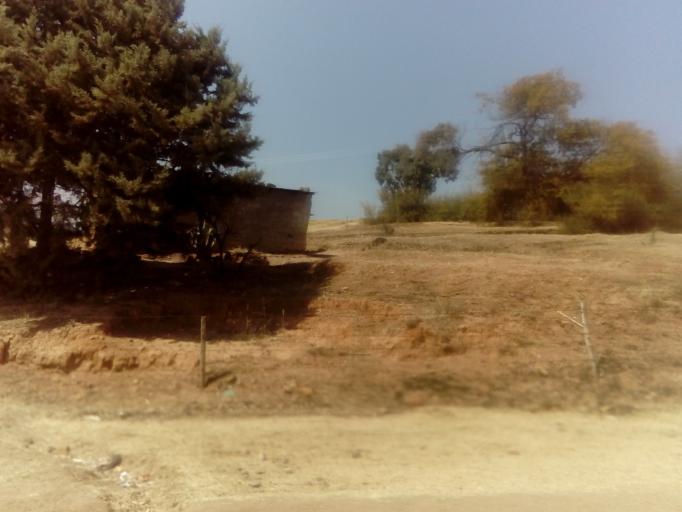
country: LS
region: Leribe
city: Leribe
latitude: -29.1308
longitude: 28.0597
